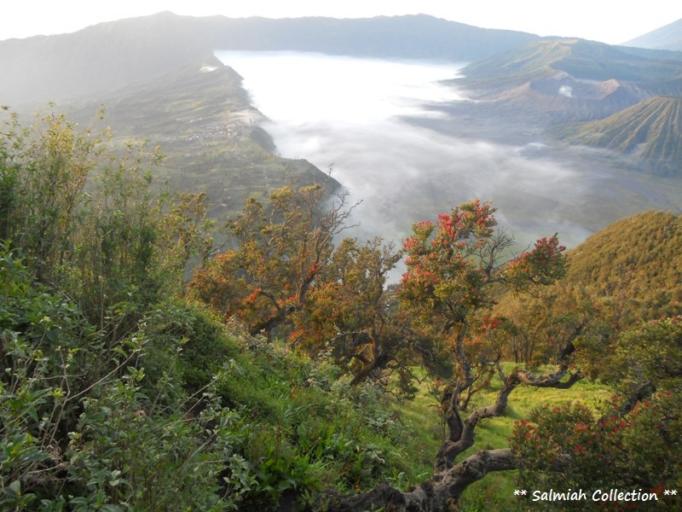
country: ID
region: East Java
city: Gubugklakah Barat
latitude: -7.9431
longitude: 112.9539
